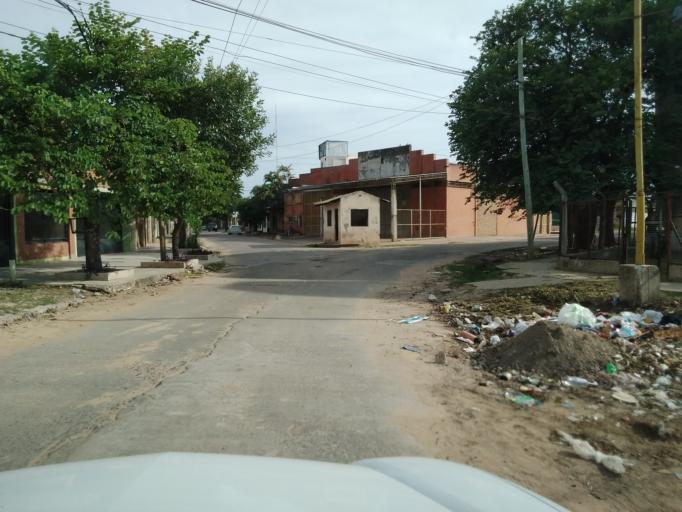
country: AR
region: Corrientes
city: Corrientes
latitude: -27.4853
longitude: -58.8458
